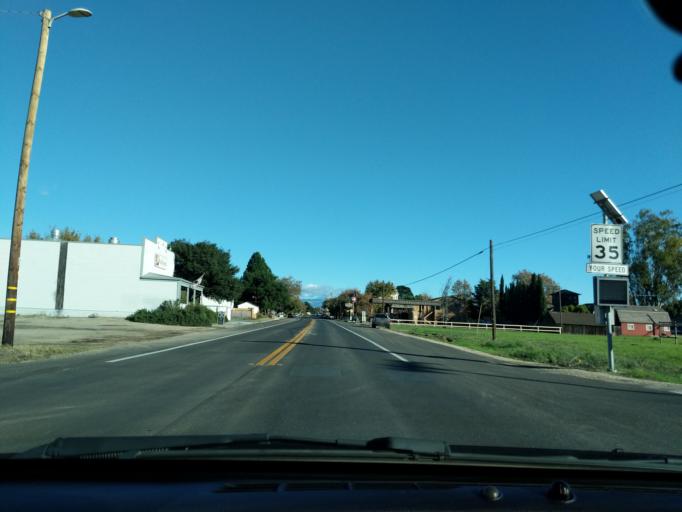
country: US
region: California
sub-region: Santa Barbara County
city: Los Alamos
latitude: 34.7443
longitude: -120.2832
